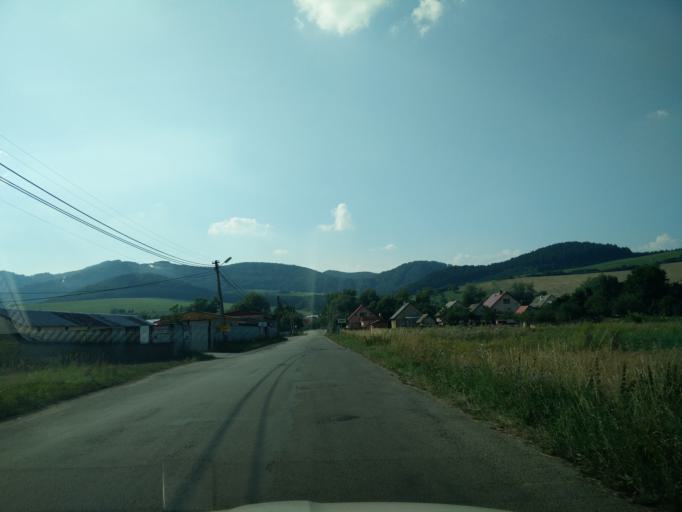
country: SK
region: Zilinsky
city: Rajec
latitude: 49.1175
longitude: 18.6546
